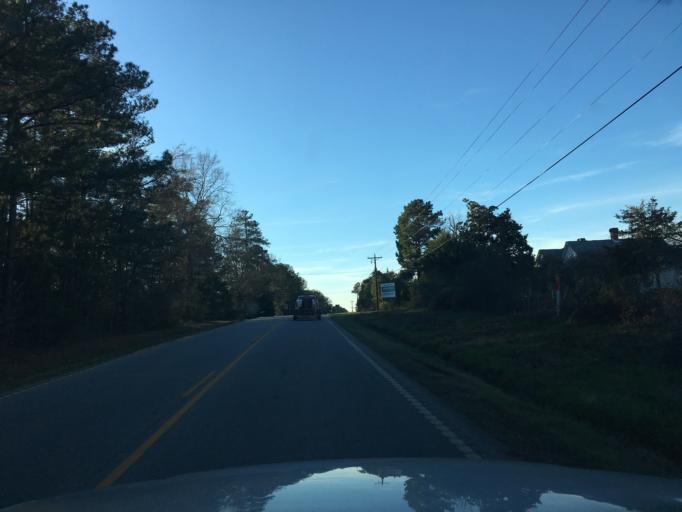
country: US
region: South Carolina
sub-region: Saluda County
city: Saluda
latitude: 34.0165
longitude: -81.7832
